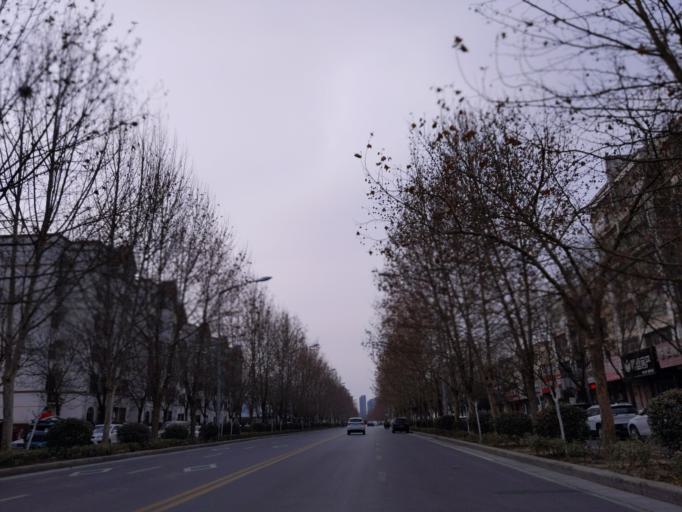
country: CN
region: Henan Sheng
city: Zhongyuanlu
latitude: 35.7575
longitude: 115.0519
